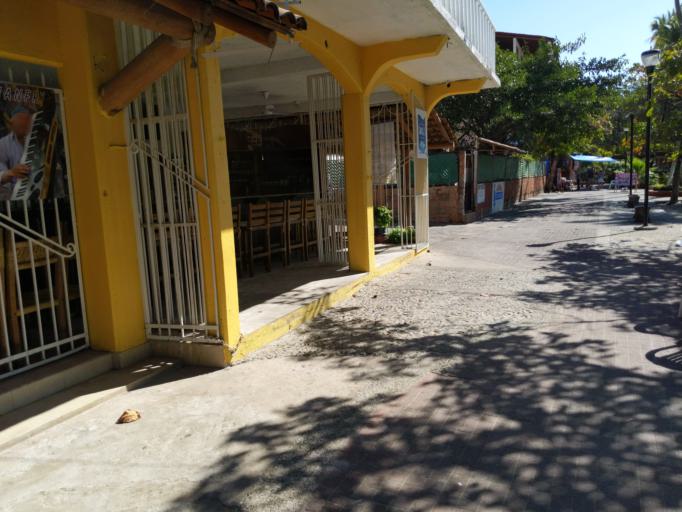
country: MX
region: Guerrero
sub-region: Zihuatanejo de Azueta
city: Ixtapa-Zihuatanejo
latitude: 17.6383
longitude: -101.5574
